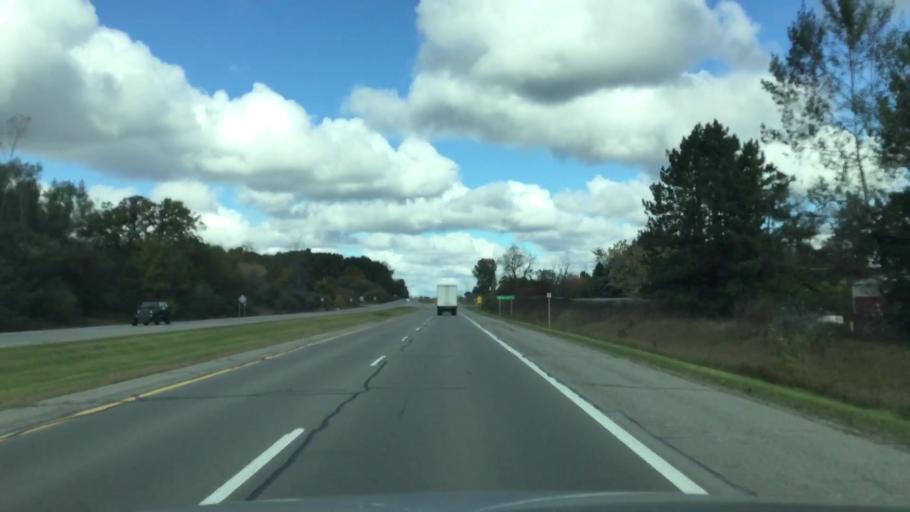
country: US
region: Michigan
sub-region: Oakland County
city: Oxford
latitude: 42.8805
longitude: -83.3032
